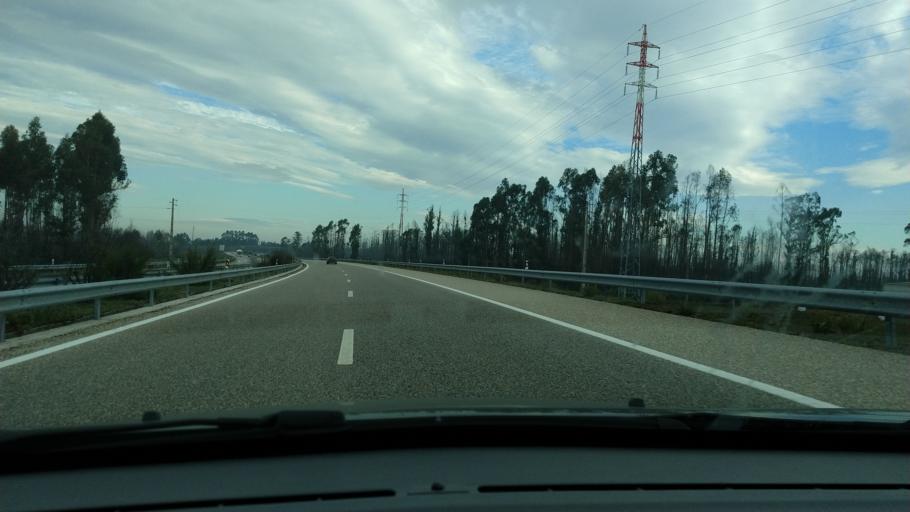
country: PT
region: Coimbra
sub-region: Mira
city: Mira
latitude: 40.4675
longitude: -8.6895
